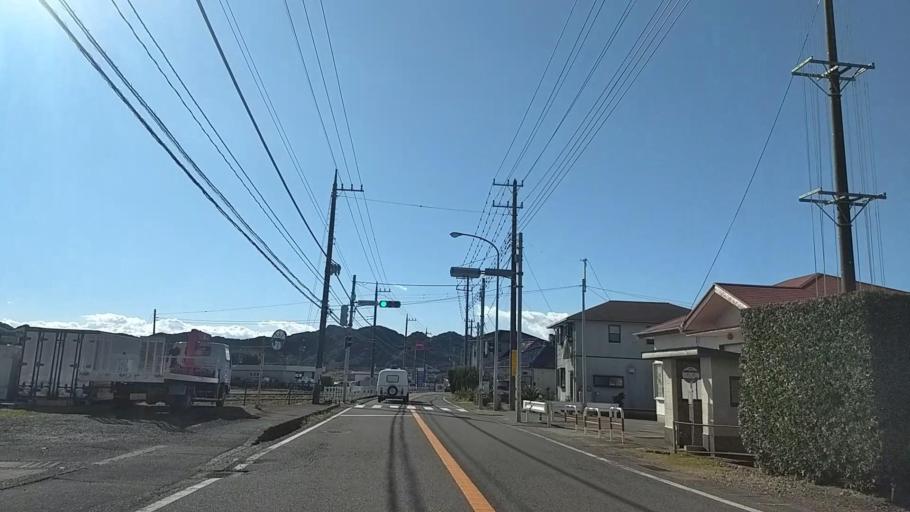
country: JP
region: Chiba
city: Tateyama
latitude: 34.9333
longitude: 139.8395
